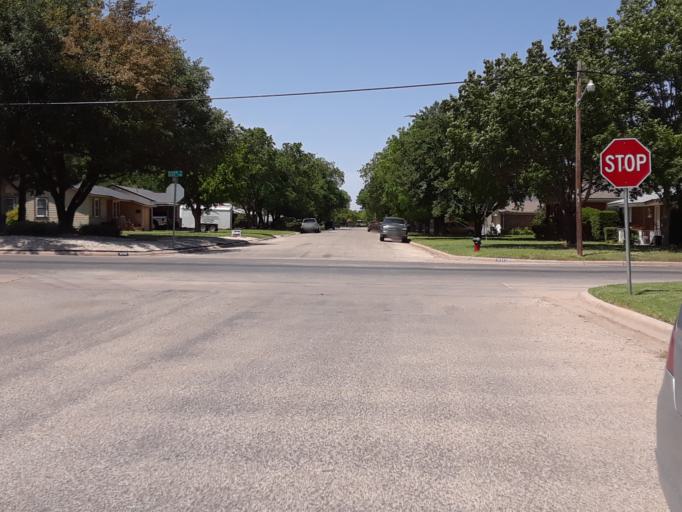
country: US
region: Texas
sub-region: Taylor County
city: Abilene
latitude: 32.4120
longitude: -99.7504
